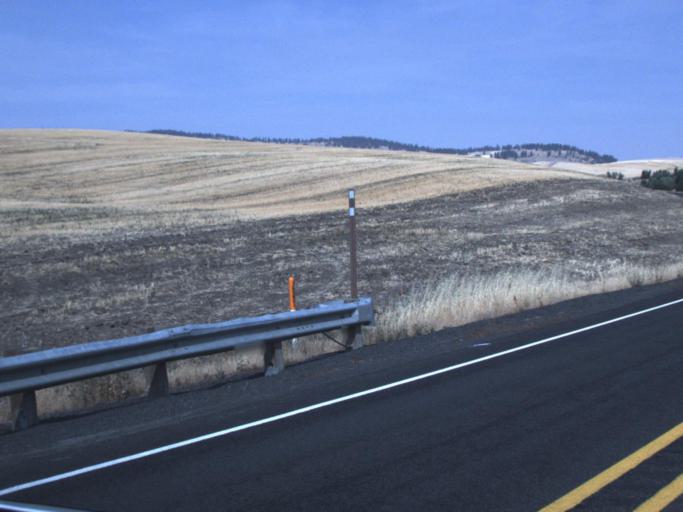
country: US
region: Washington
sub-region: Whitman County
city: Pullman
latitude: 46.8278
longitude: -117.1147
